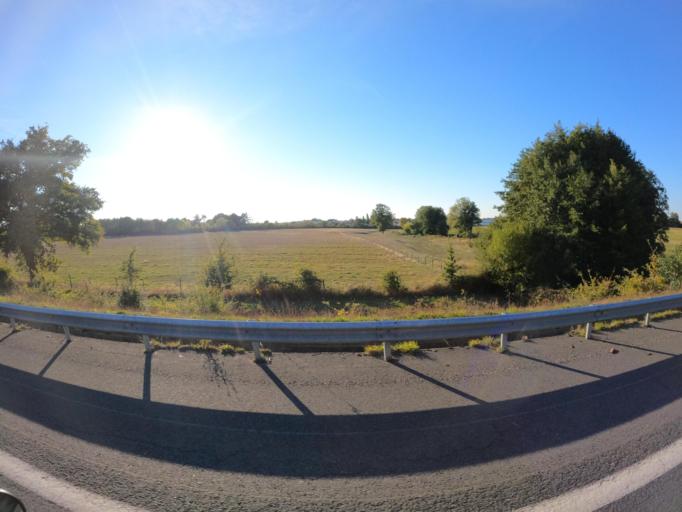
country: FR
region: Pays de la Loire
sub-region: Departement de Maine-et-Loire
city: Mazieres-en-Mauges
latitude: 47.0763
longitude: -0.8261
